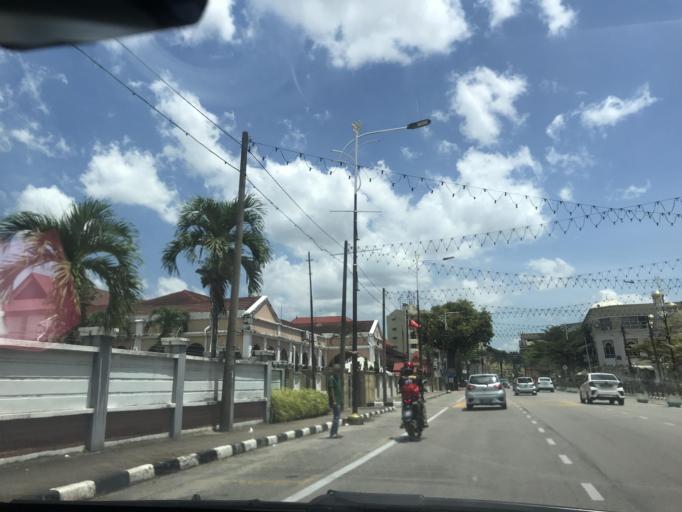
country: MY
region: Kelantan
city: Kota Bharu
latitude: 6.1253
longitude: 102.2394
